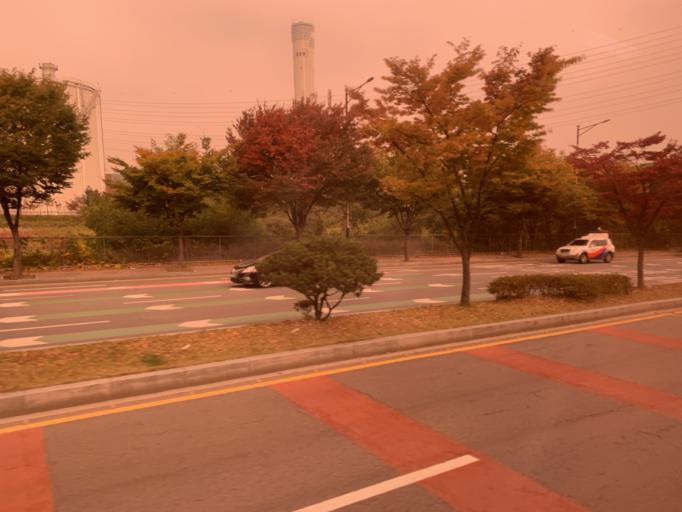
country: KR
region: Gyeonggi-do
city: Osan
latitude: 37.2170
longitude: 127.0823
